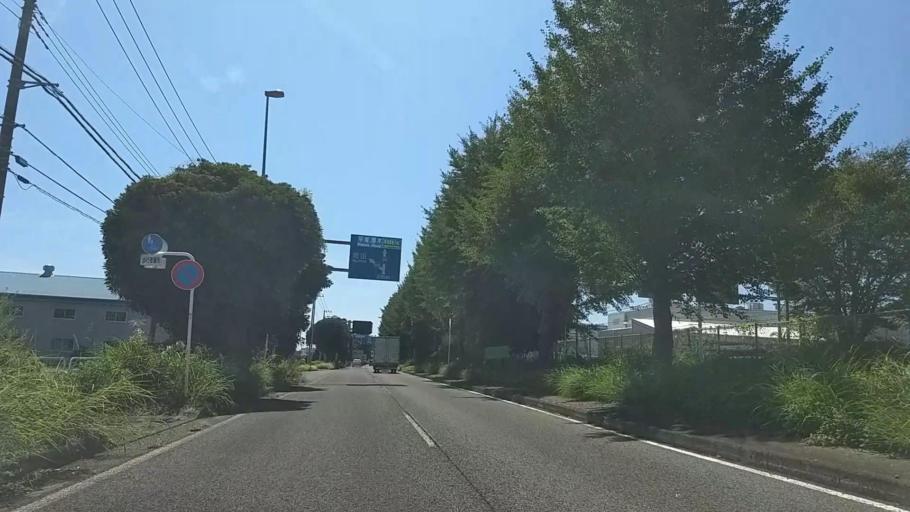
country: JP
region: Kanagawa
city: Zama
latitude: 35.5404
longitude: 139.3612
